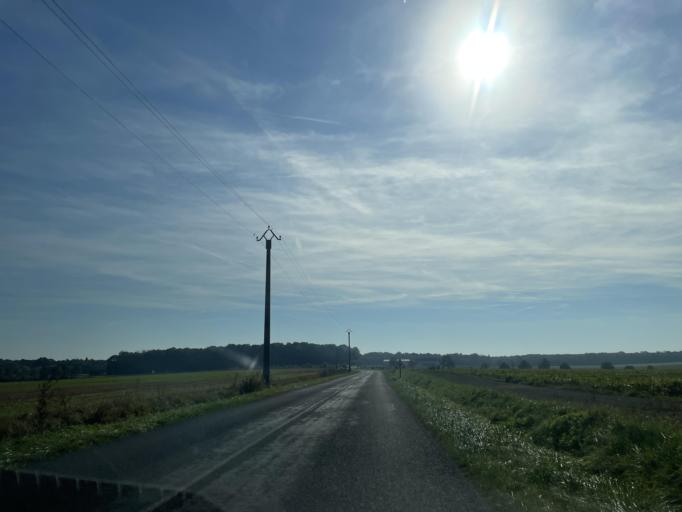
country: FR
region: Ile-de-France
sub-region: Departement de Seine-et-Marne
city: Saint-Jean-les-Deux-Jumeaux
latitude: 48.9268
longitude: 3.0003
